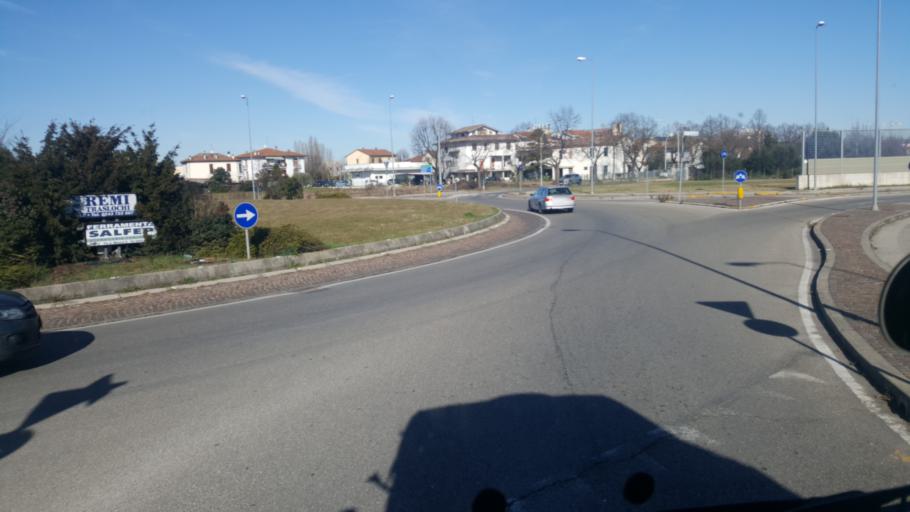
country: IT
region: Emilia-Romagna
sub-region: Forli-Cesena
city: Forli
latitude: 44.2443
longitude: 12.0795
